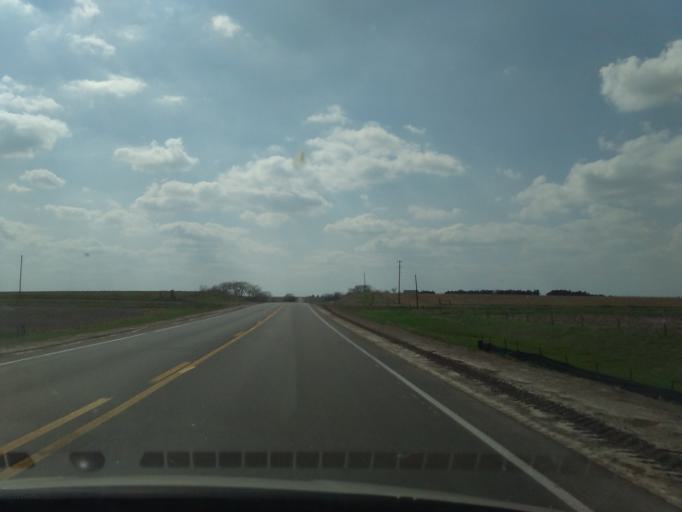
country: US
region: Nebraska
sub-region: Nuckolls County
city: Superior
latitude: 40.0895
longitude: -98.0842
